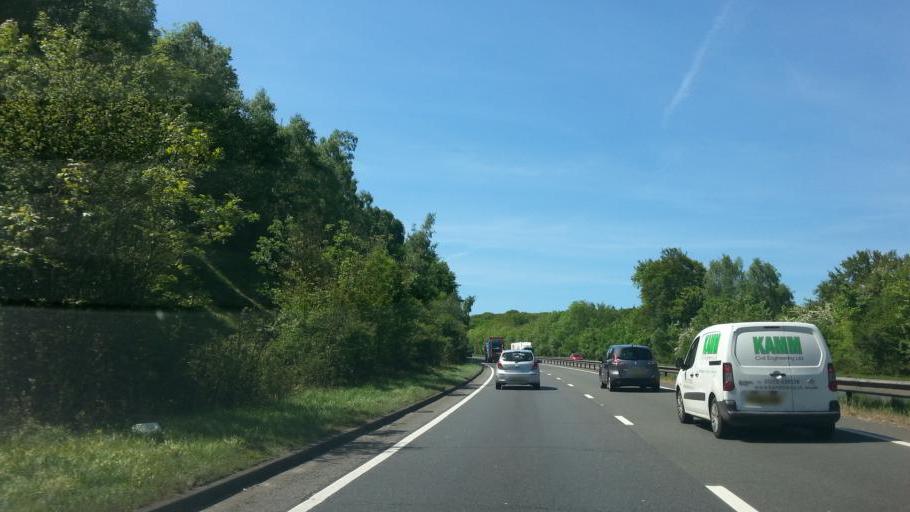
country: GB
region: England
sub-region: Hampshire
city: Andover
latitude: 51.1954
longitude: -1.4239
